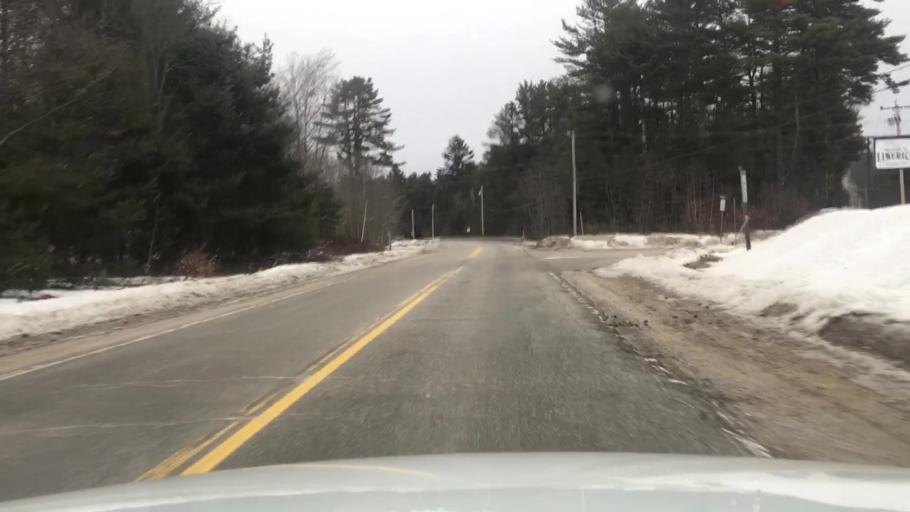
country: US
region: Maine
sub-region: York County
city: Newfield
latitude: 43.6540
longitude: -70.8386
